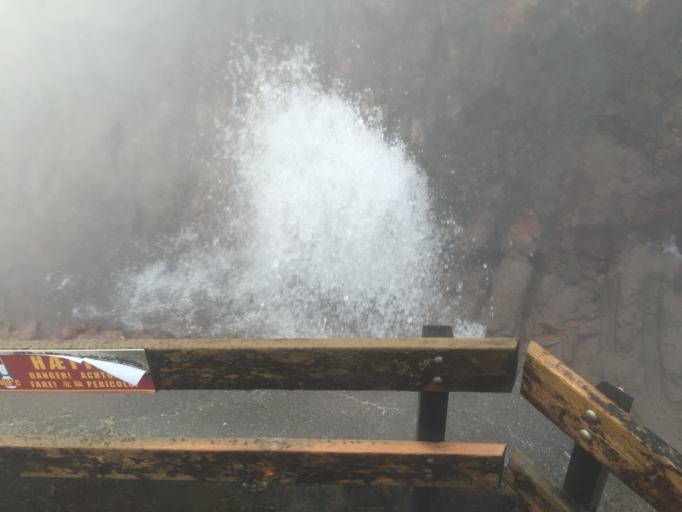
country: IS
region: West
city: Borgarnes
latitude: 64.6635
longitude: -21.4107
